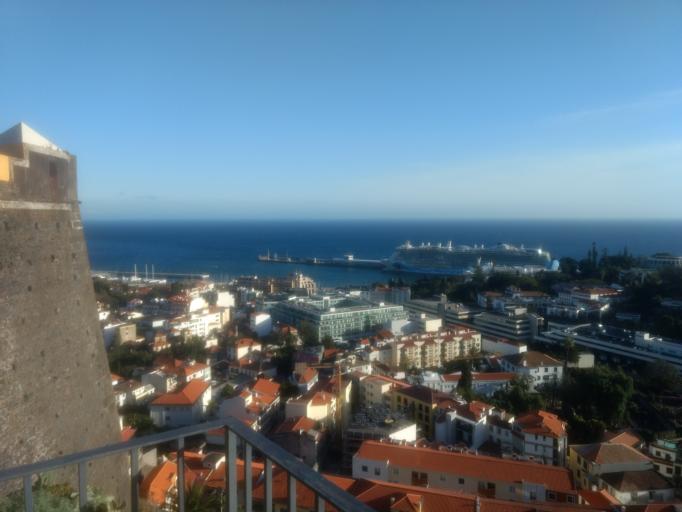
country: PT
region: Madeira
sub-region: Funchal
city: Nossa Senhora do Monte
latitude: 32.6506
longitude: -16.9165
